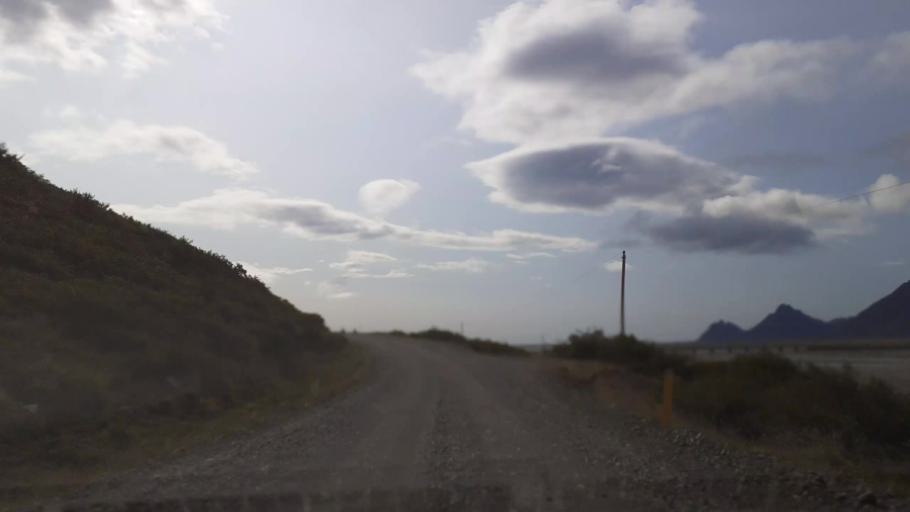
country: IS
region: East
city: Hoefn
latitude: 64.4261
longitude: -14.8830
